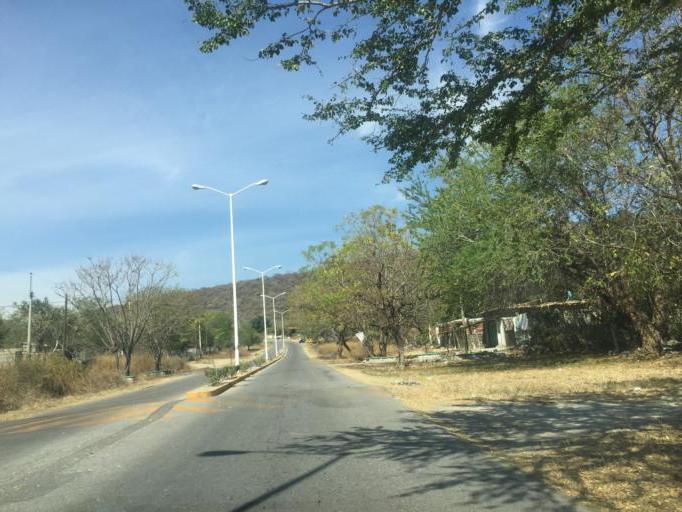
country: MX
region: Morelos
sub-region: Miacatlan
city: Xochicalco (Cirenio Longares)
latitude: 18.7909
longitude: -99.2974
